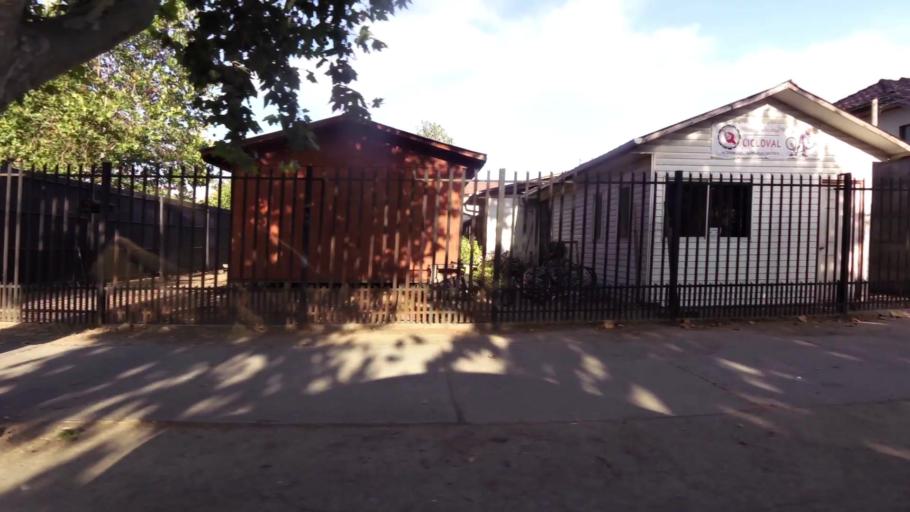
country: CL
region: Maule
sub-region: Provincia de Talca
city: Talca
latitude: -35.4168
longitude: -71.6603
